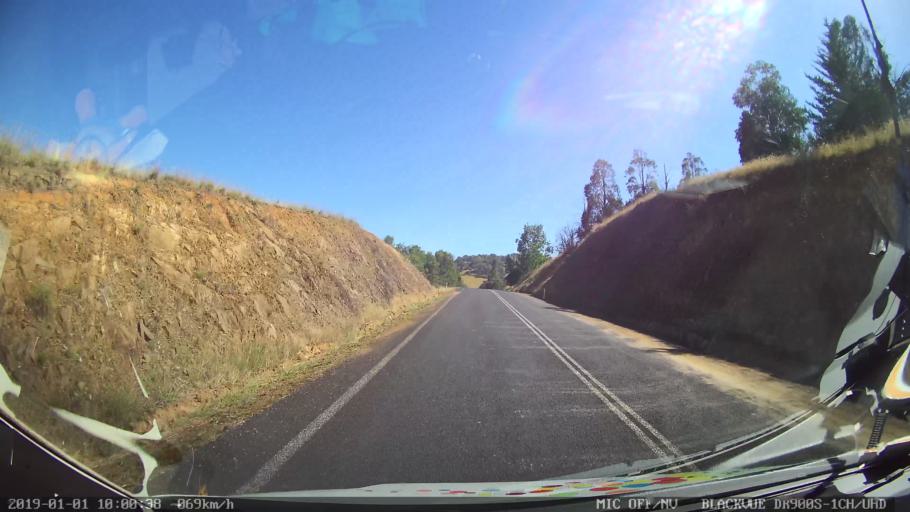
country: AU
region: New South Wales
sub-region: Snowy River
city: Jindabyne
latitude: -36.2000
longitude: 148.1022
